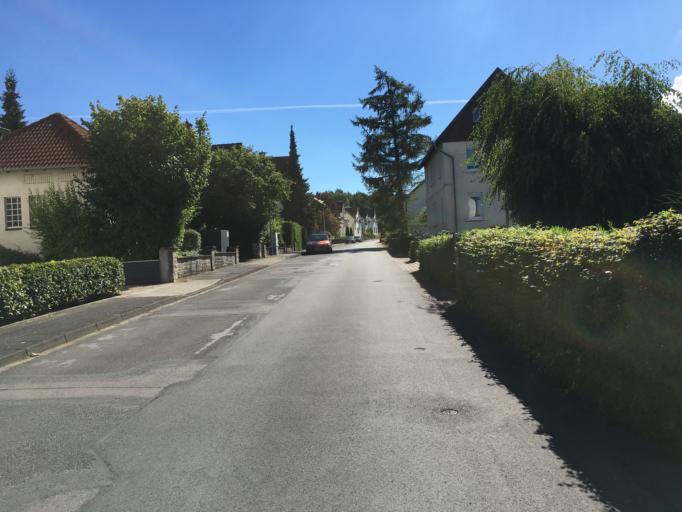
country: DE
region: North Rhine-Westphalia
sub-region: Regierungsbezirk Detmold
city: Detmold
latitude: 51.9290
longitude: 8.8447
